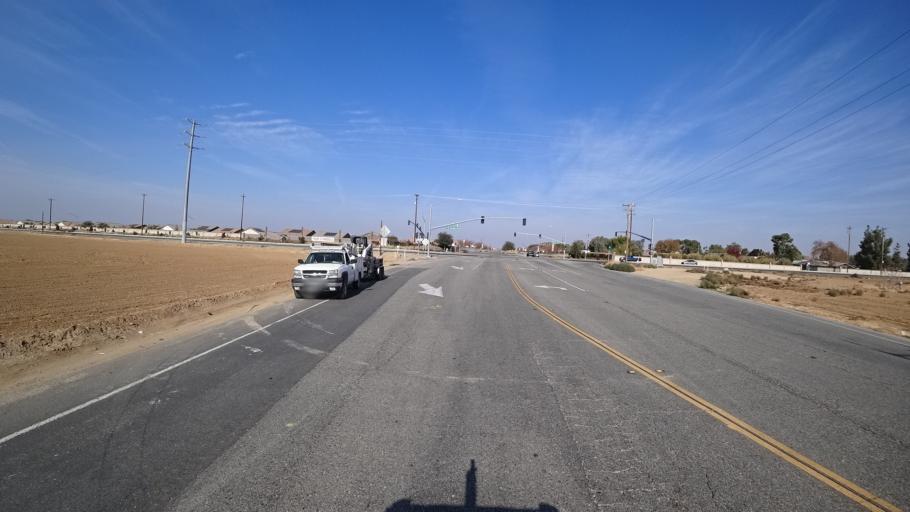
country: US
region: California
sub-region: Kern County
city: Greenacres
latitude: 35.4406
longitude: -119.1100
